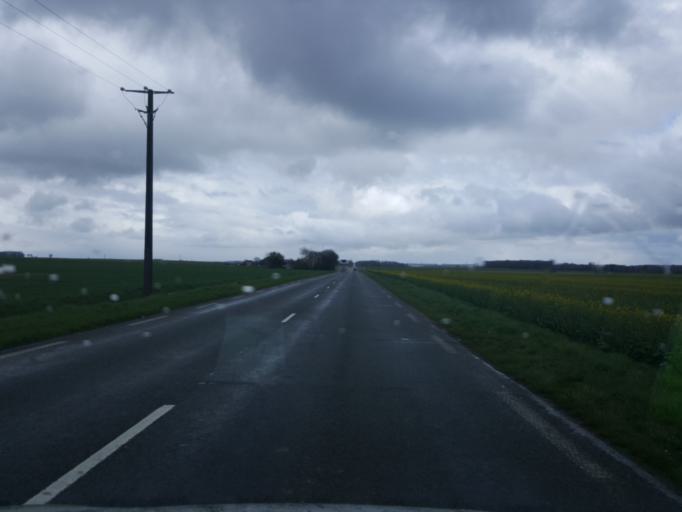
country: FR
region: Picardie
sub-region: Departement de l'Oise
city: Trie-Chateau
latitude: 49.2877
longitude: 1.8431
